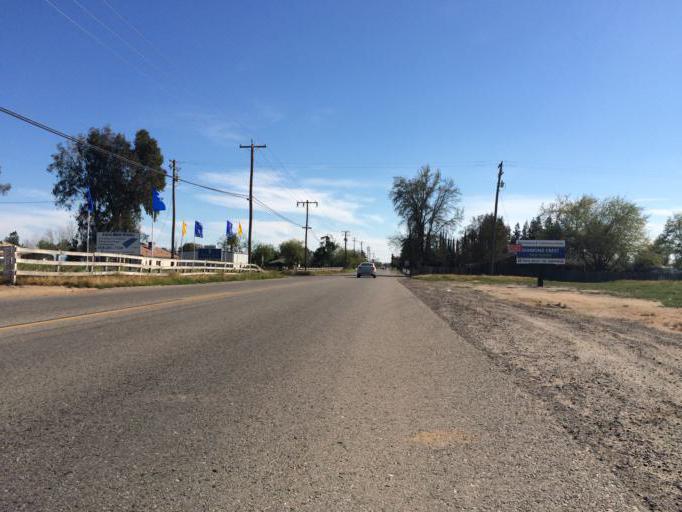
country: US
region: California
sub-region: Fresno County
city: Clovis
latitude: 36.8599
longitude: -119.6841
